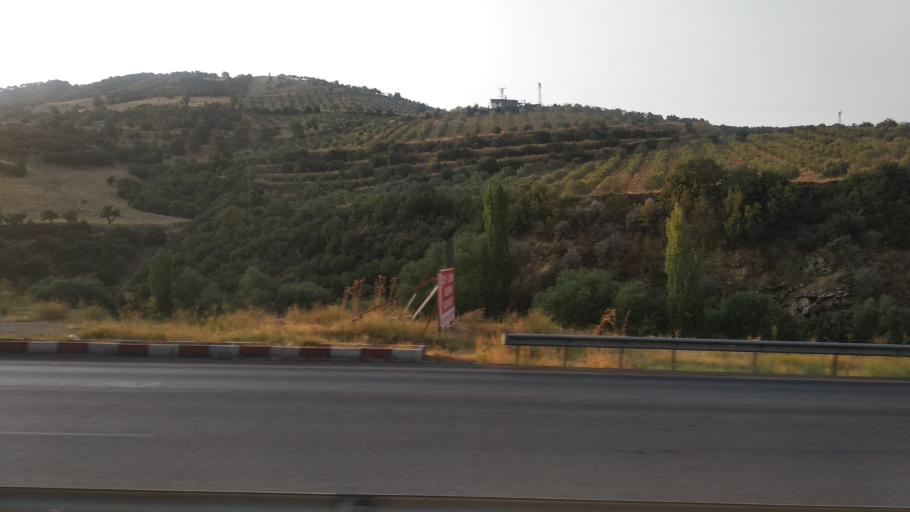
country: TR
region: Manisa
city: Menye
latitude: 38.5473
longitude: 28.4541
